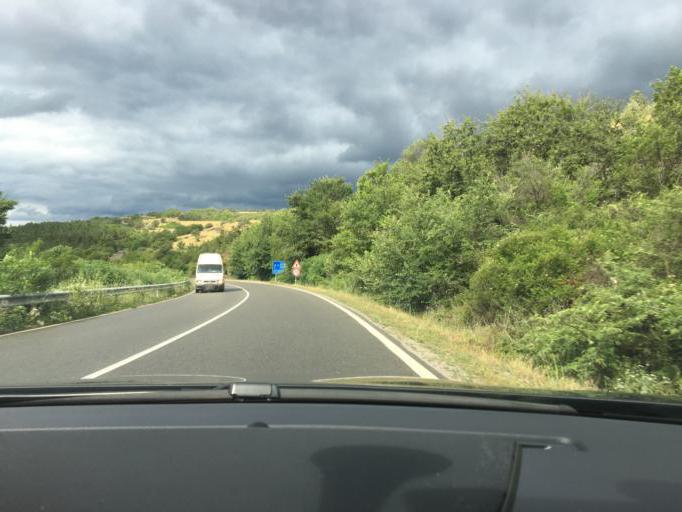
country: BG
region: Kyustendil
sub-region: Obshtina Bobovdol
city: Bobovdol
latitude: 42.2652
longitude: 22.9220
